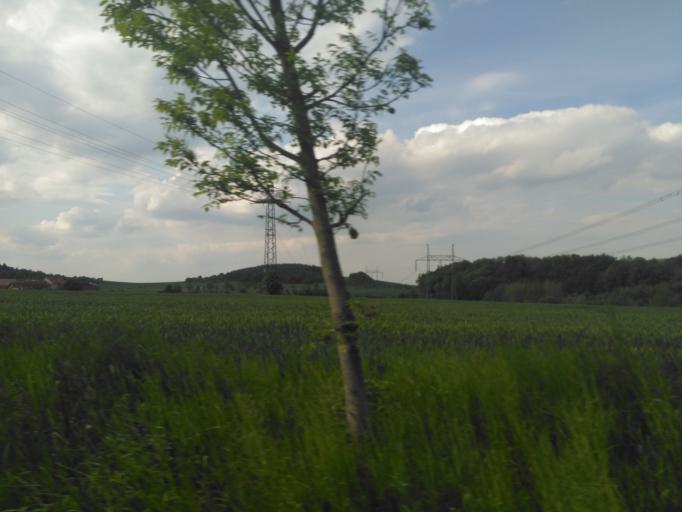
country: CZ
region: Central Bohemia
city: Chynava
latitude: 50.0067
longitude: 14.0966
